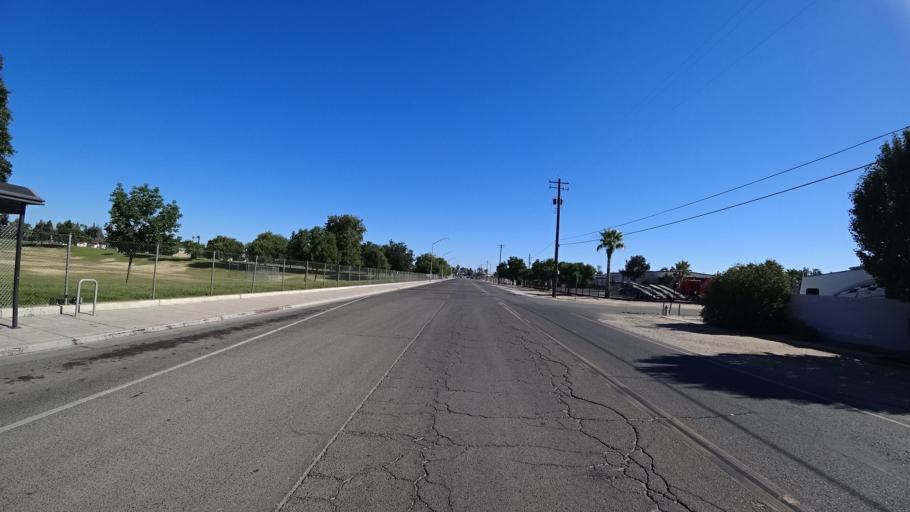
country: US
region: California
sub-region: Fresno County
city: West Park
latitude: 36.7617
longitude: -119.8356
